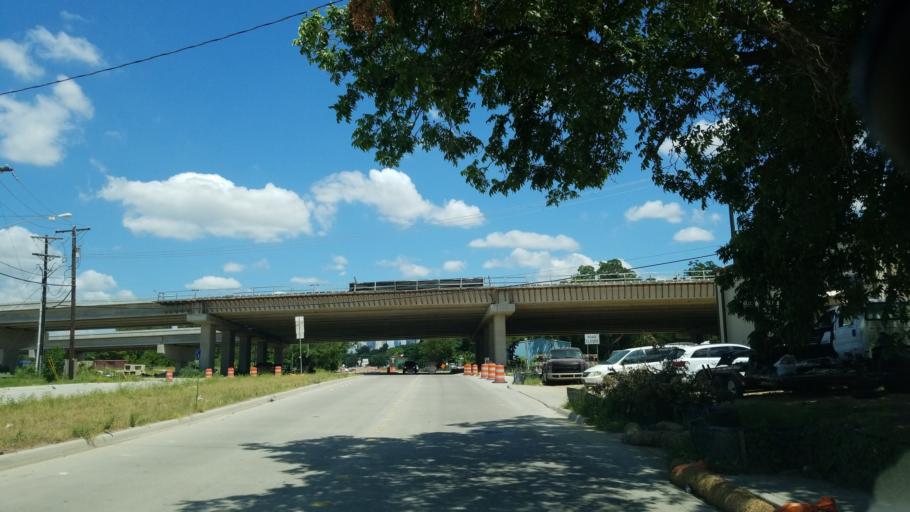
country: US
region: Texas
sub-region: Dallas County
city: Dallas
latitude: 32.7443
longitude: -96.7601
